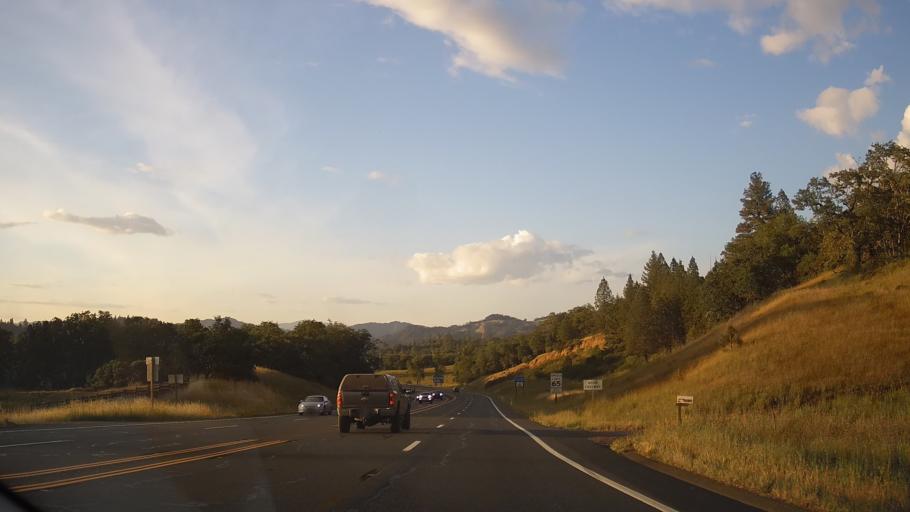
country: US
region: California
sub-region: Mendocino County
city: Willits
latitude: 39.3593
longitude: -123.3163
